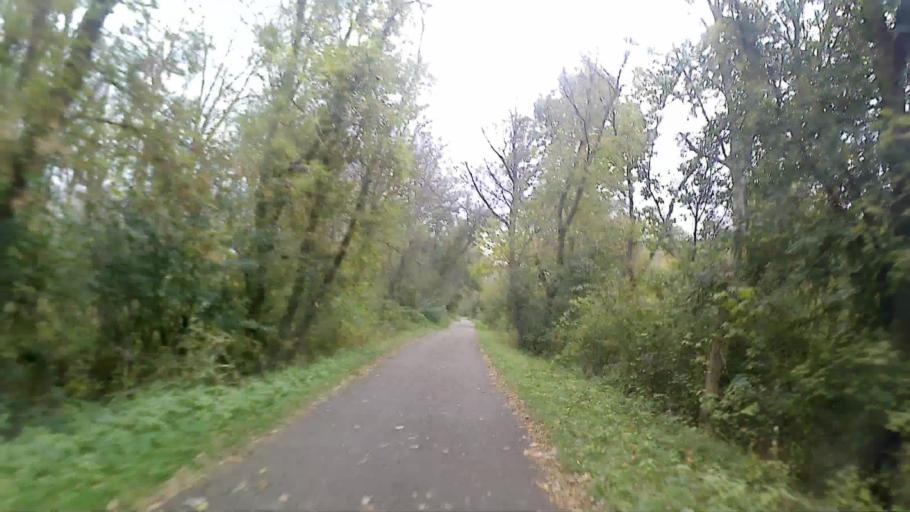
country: US
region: Illinois
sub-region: Kane County
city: Sugar Grove
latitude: 41.7758
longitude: -88.4180
